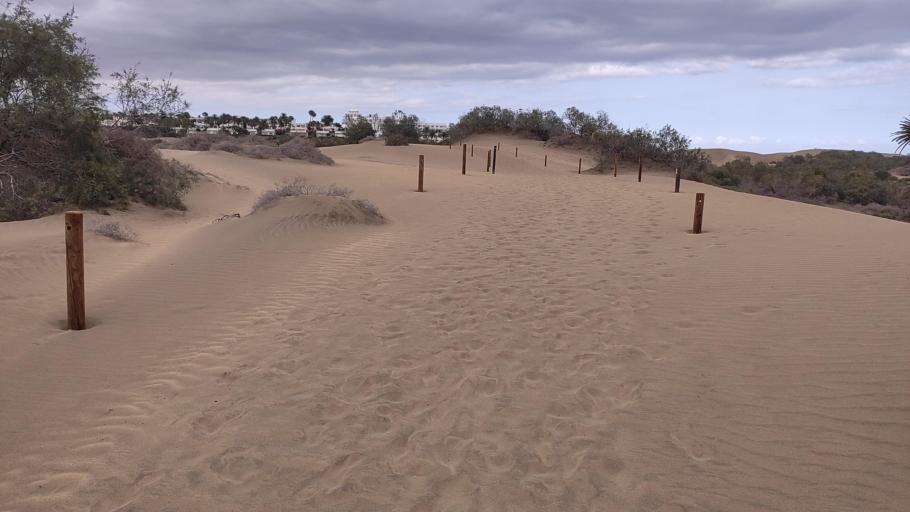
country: ES
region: Canary Islands
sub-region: Provincia de Las Palmas
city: Playa del Ingles
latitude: 27.7449
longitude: -15.5827
